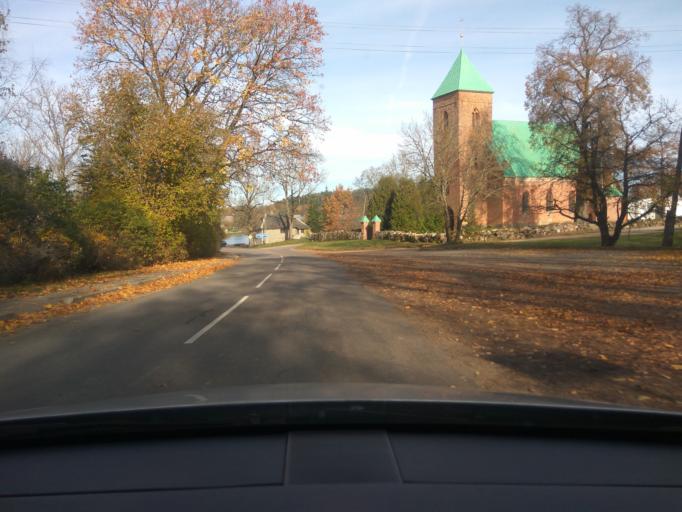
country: LV
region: Alsunga
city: Alsunga
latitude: 57.0166
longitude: 21.6885
